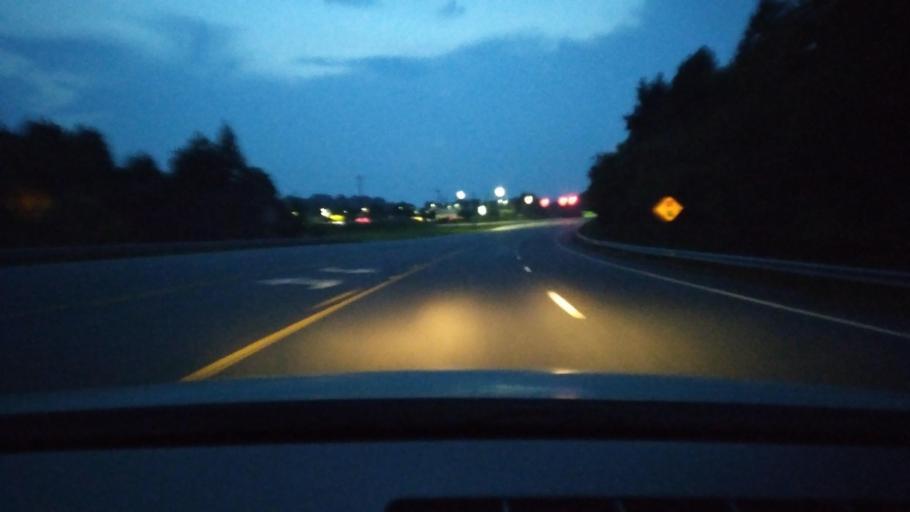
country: US
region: North Carolina
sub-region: Rockingham County
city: Reidsville
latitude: 36.3786
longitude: -79.6598
